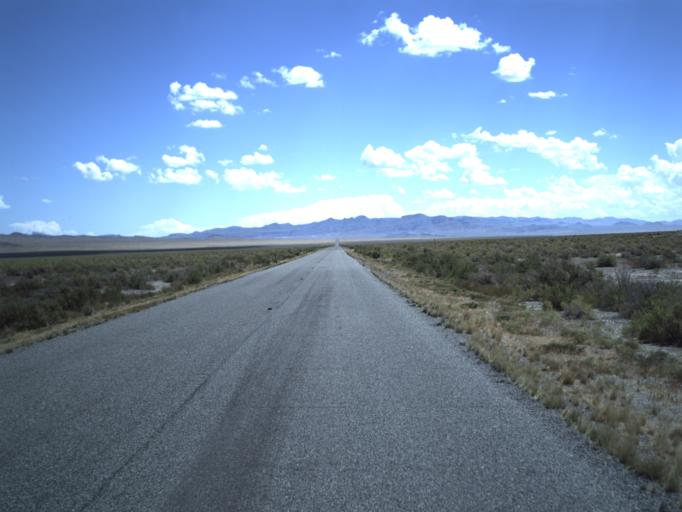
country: US
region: Nevada
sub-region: White Pine County
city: McGill
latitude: 39.0488
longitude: -113.9407
